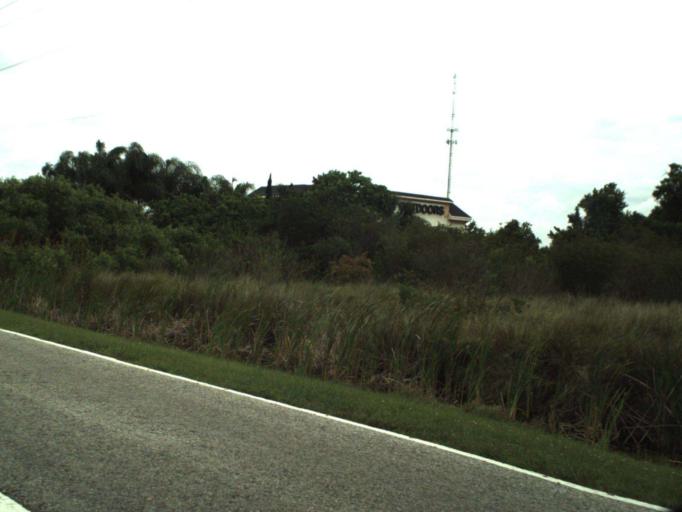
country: US
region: Florida
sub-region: Brevard County
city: Titusville
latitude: 28.5505
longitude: -80.8622
